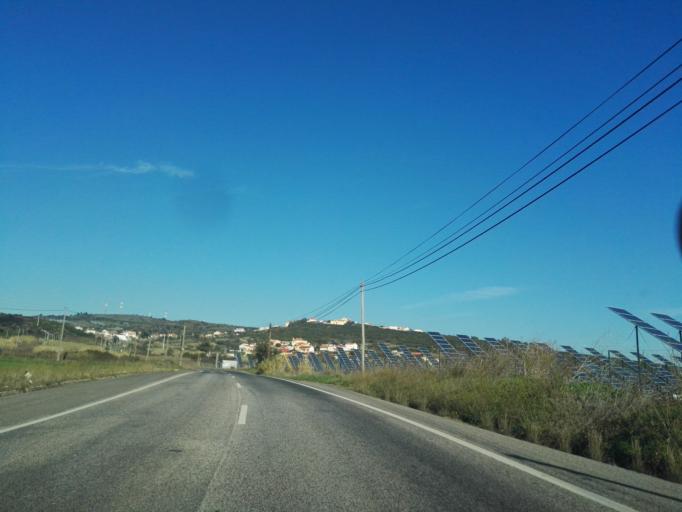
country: PT
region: Lisbon
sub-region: Loures
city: Loures
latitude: 38.8585
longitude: -9.1817
